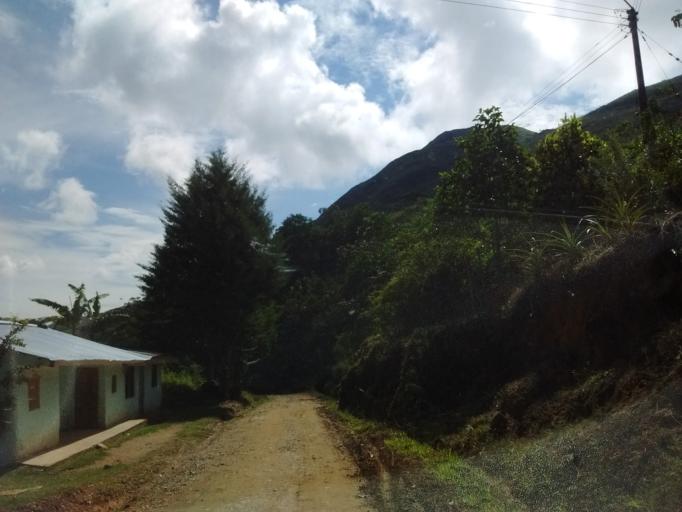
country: CO
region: Cauca
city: Morales
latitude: 2.6967
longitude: -76.7473
